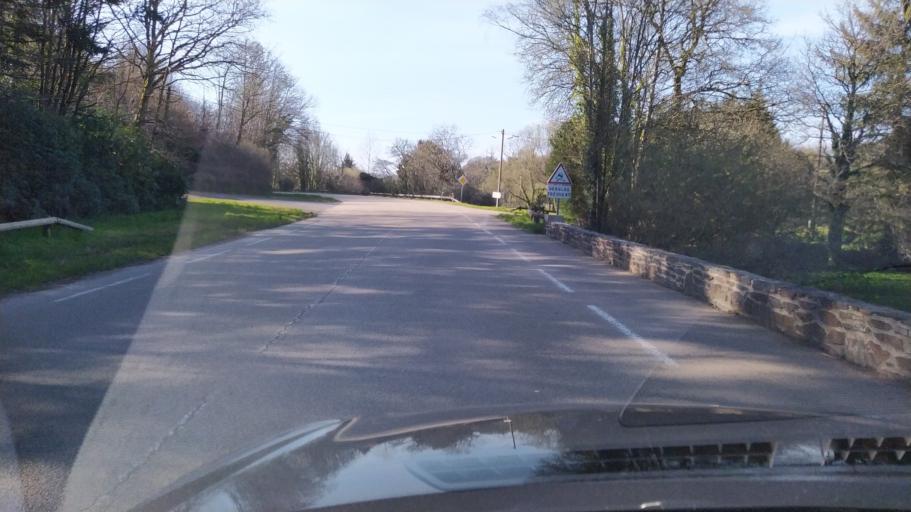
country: FR
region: Brittany
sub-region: Departement du Finistere
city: Lampaul-Guimiliau
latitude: 48.4950
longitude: -4.0482
